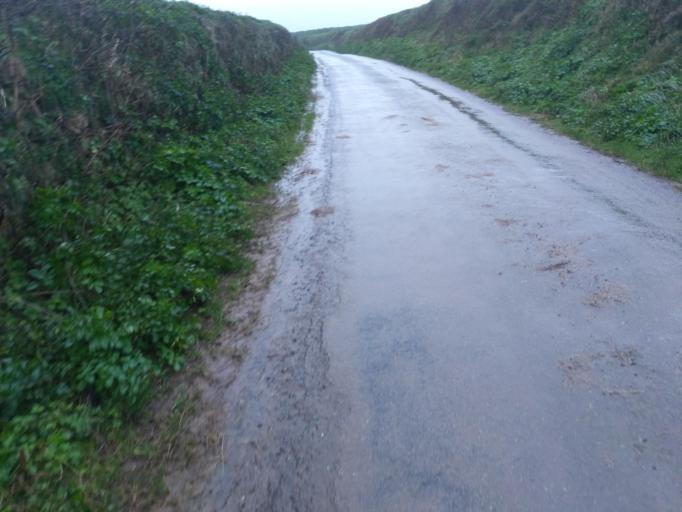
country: GB
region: England
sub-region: Cornwall
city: Torpoint
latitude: 50.3346
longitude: -4.2184
